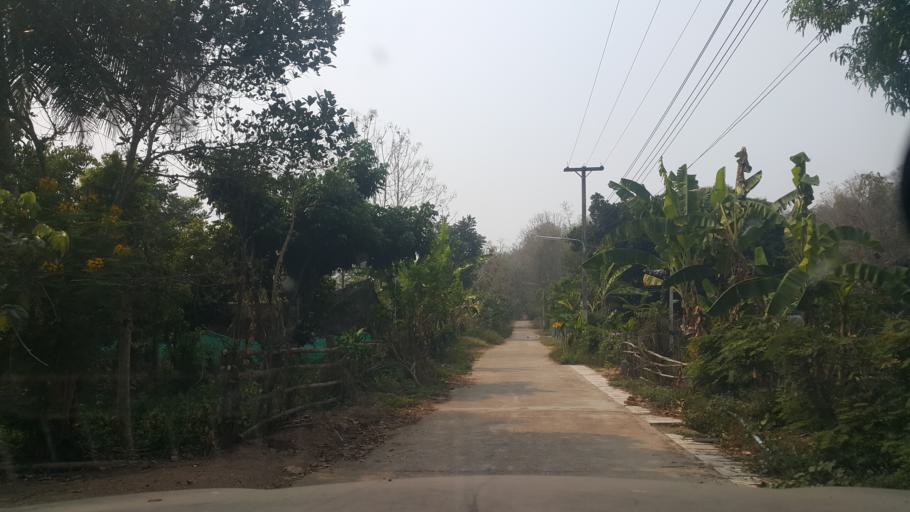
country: TH
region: Chiang Mai
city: Mae On
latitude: 18.6798
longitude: 99.2929
